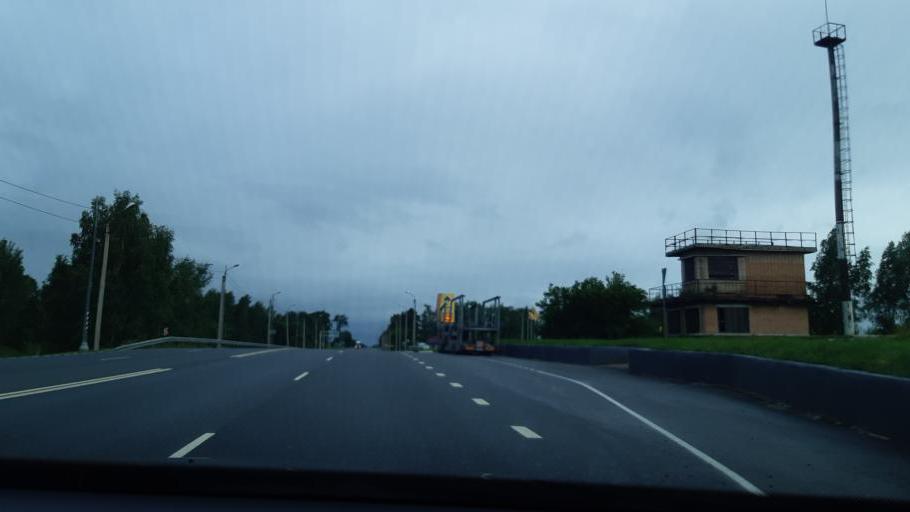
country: RU
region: Smolensk
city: Oster
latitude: 53.9847
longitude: 32.8246
